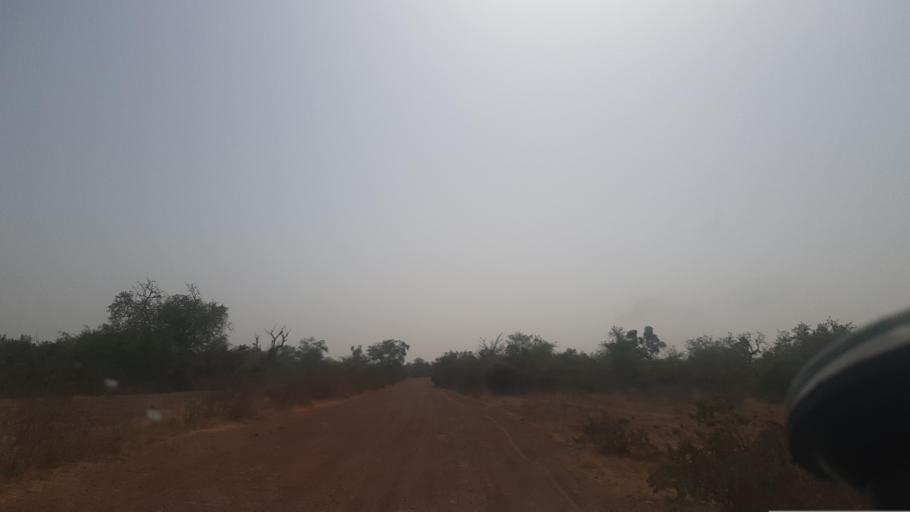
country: ML
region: Segou
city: Baroueli
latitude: 13.0655
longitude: -6.4769
